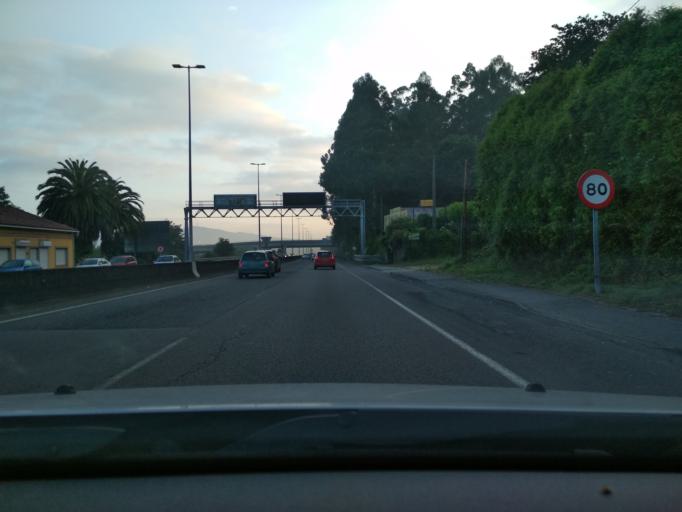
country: ES
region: Galicia
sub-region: Provincia da Coruna
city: Santiago de Compostela
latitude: 42.8498
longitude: -8.5732
